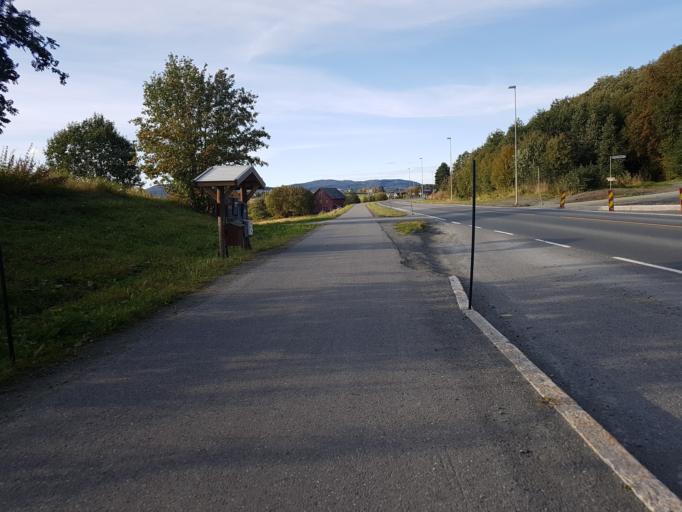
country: NO
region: Sor-Trondelag
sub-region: Trondheim
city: Trondheim
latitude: 63.3724
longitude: 10.4327
